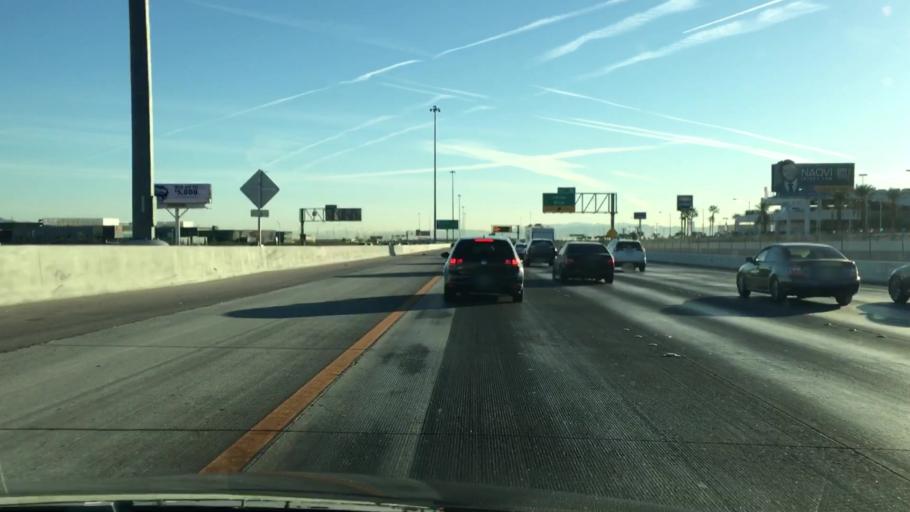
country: US
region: Nevada
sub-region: Clark County
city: Enterprise
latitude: 36.0666
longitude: -115.2367
